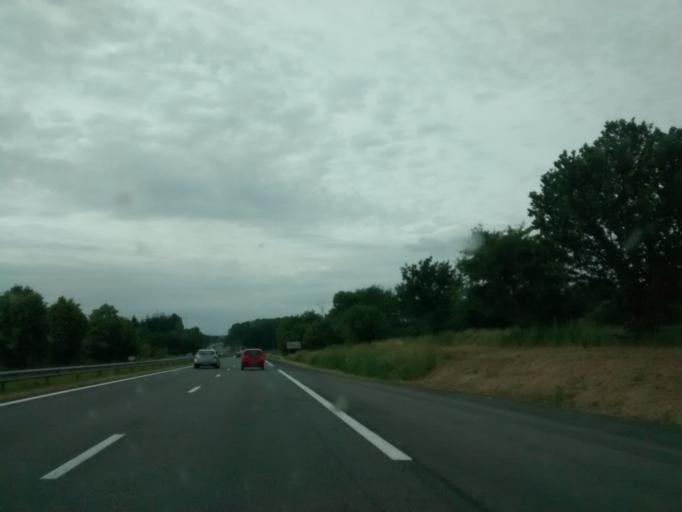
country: FR
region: Brittany
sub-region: Departement d'Ille-et-Vilaine
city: Quedillac
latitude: 48.2431
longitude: -2.1299
